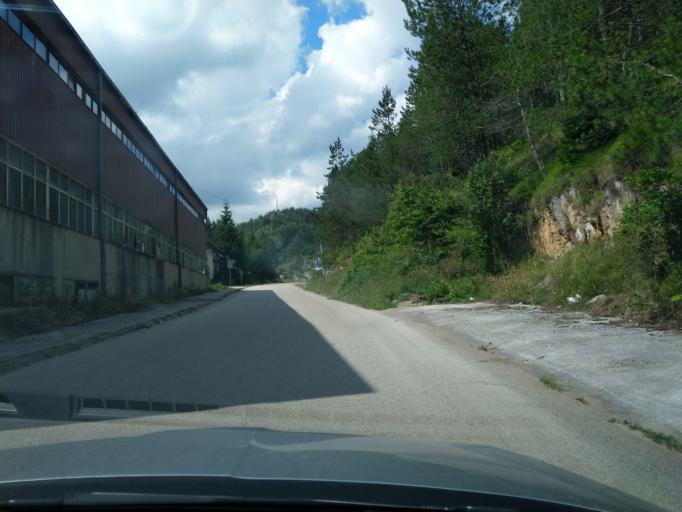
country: RS
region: Central Serbia
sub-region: Zlatiborski Okrug
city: Nova Varos
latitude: 43.5484
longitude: 19.9027
